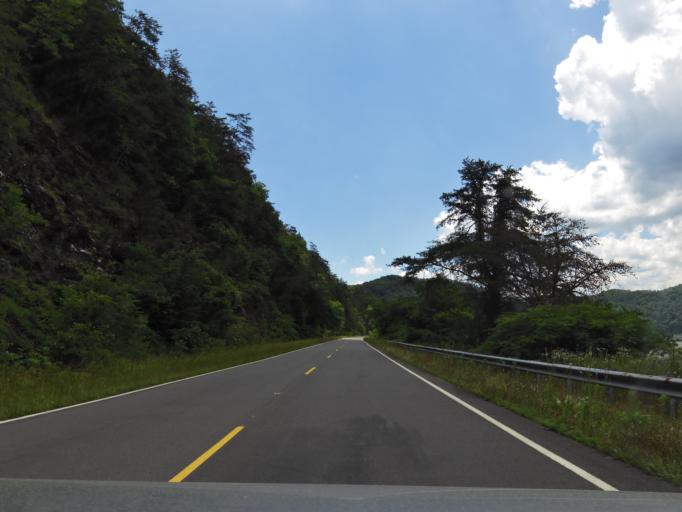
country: US
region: Tennessee
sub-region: Loudon County
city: Greenback
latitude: 35.5379
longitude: -83.9946
